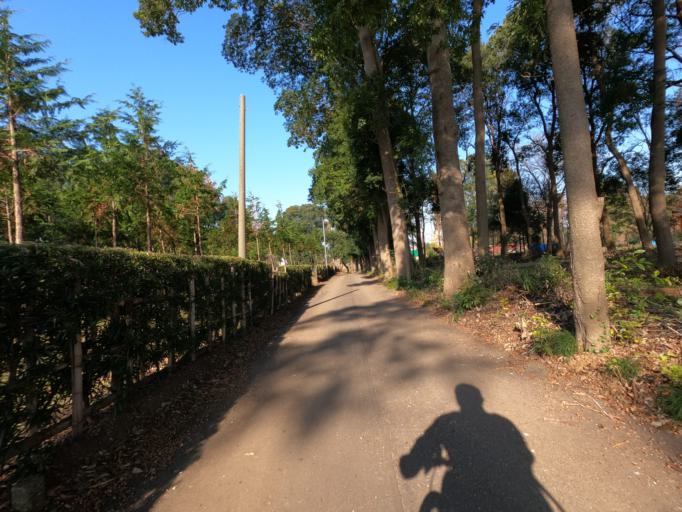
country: JP
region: Ibaraki
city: Moriya
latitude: 35.9472
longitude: 139.9740
